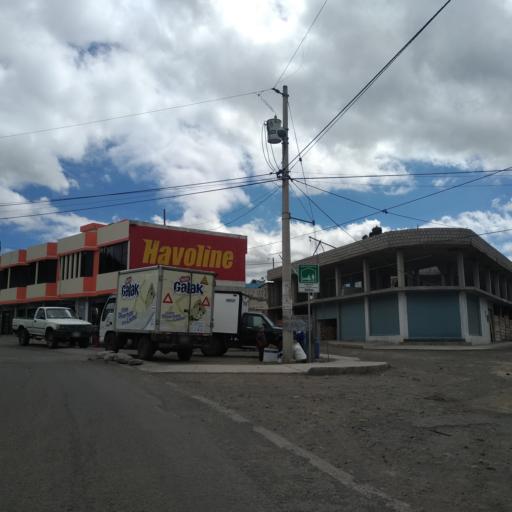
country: EC
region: Cotopaxi
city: Saquisili
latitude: -0.7481
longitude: -78.7215
